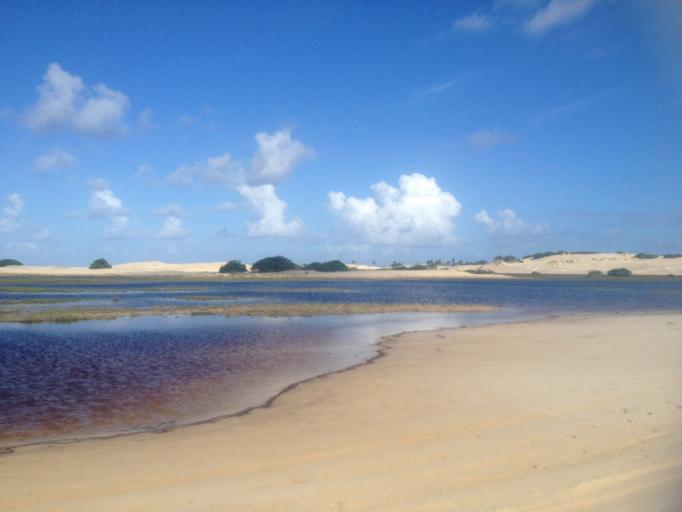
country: BR
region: Sergipe
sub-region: Indiaroba
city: Indiaroba
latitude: -11.4762
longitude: -37.3753
